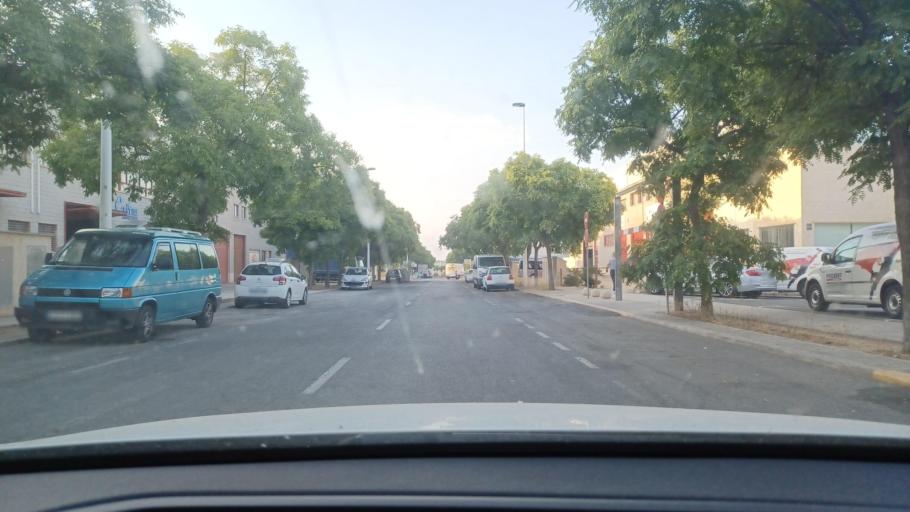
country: ES
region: Valencia
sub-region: Provincia de Alicante
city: Elche
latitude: 38.2948
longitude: -0.6201
